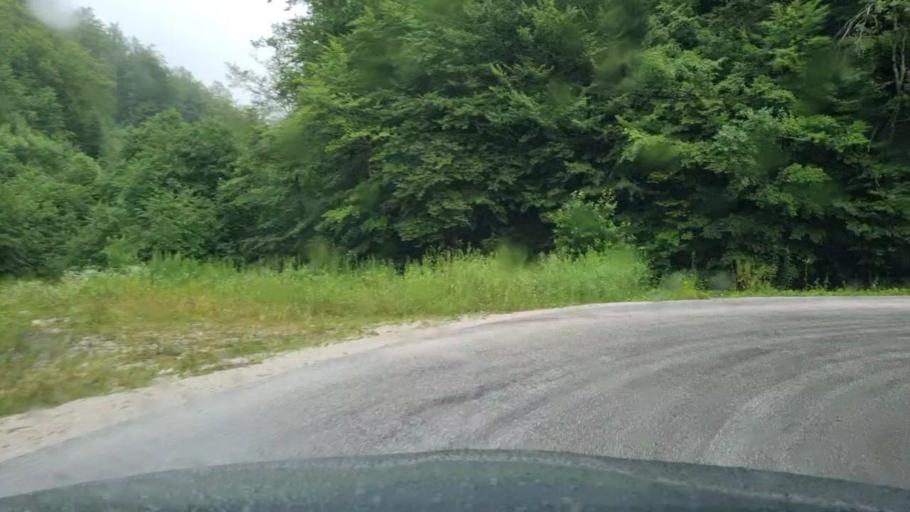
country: BA
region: Republika Srpska
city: Koran
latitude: 43.6487
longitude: 18.6054
